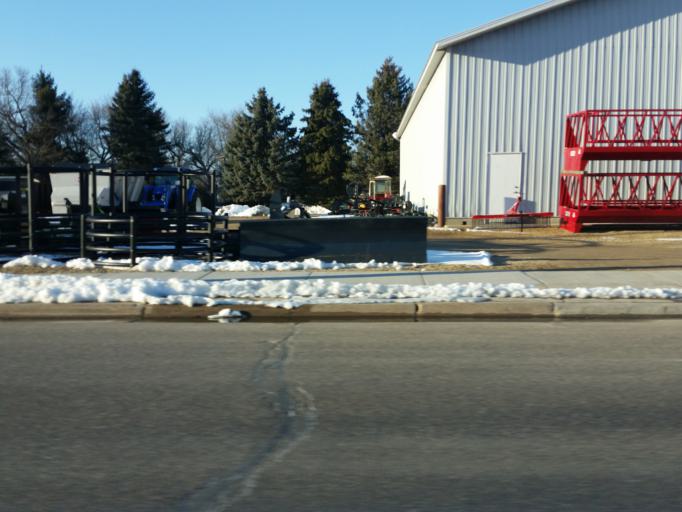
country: US
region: Minnesota
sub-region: Dakota County
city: Hastings
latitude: 44.6736
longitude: -92.9642
